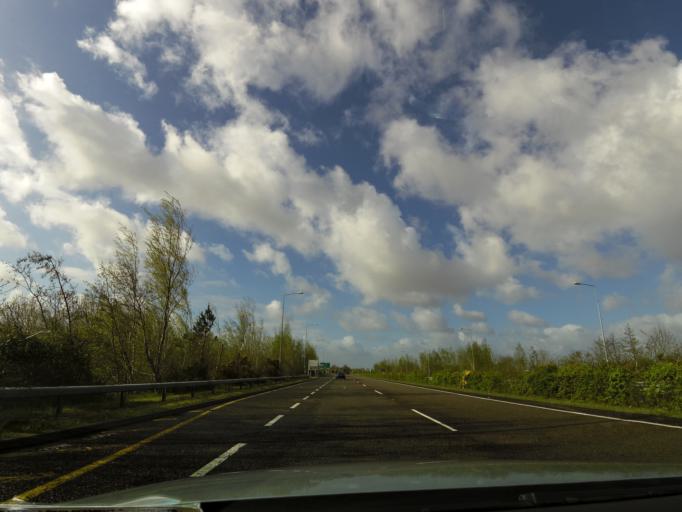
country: IE
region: Munster
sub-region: An Clar
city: Shannon
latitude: 52.7181
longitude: -8.8809
